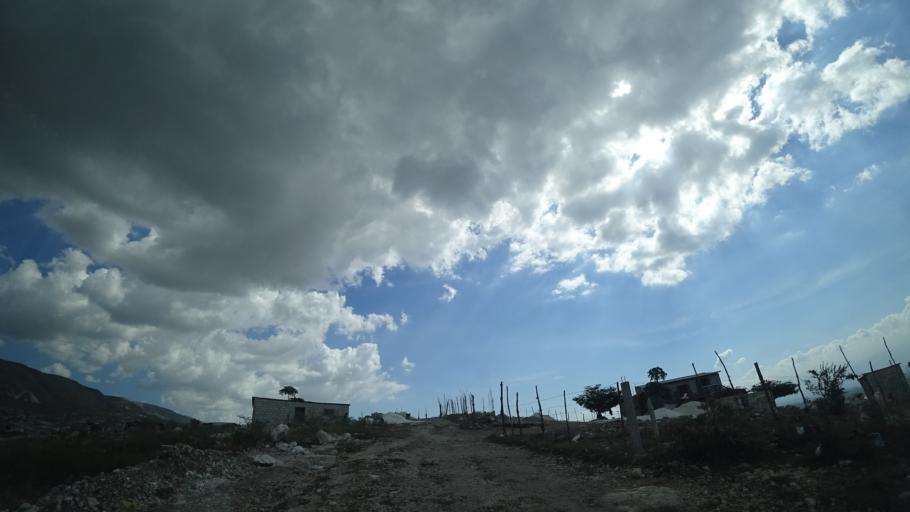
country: HT
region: Ouest
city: Cabaret
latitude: 18.6784
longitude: -72.3131
